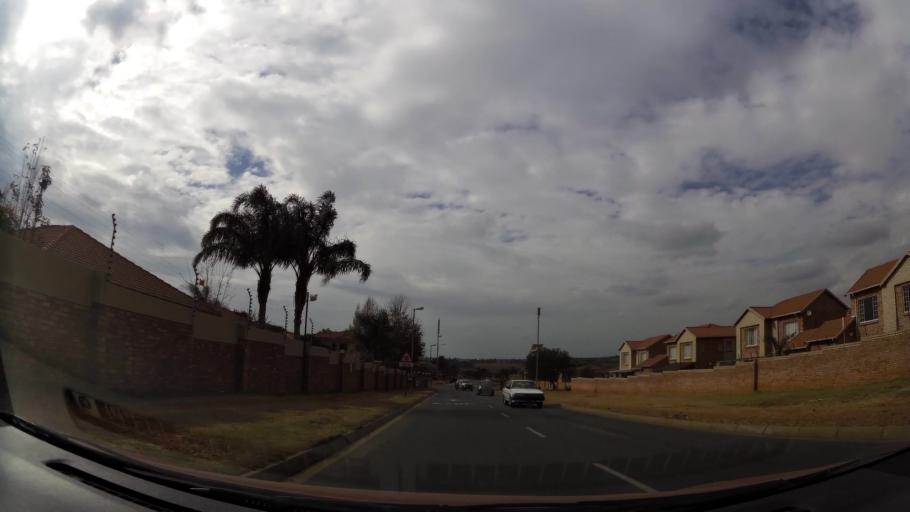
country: ZA
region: Gauteng
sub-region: City of Johannesburg Metropolitan Municipality
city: Roodepoort
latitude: -26.0960
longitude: 27.8772
